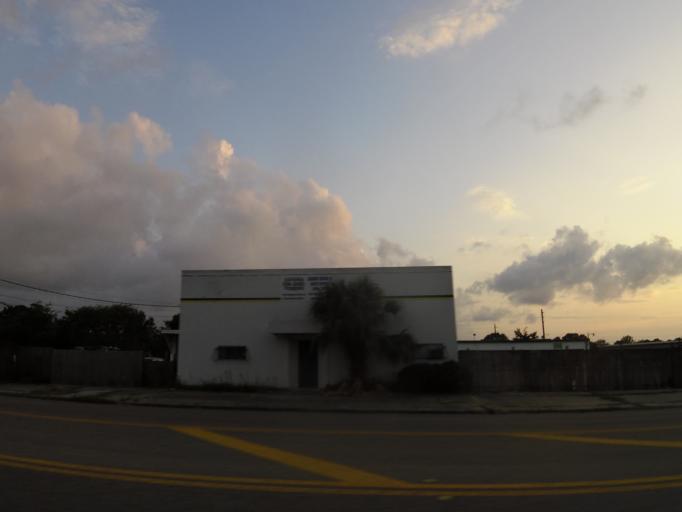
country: US
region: Florida
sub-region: Duval County
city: Jacksonville
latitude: 30.3227
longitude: -81.7287
